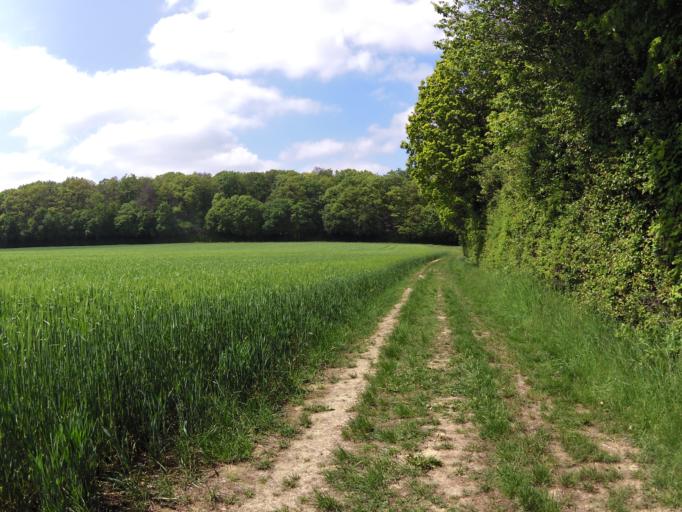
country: DE
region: Bavaria
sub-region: Regierungsbezirk Unterfranken
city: Reichenberg
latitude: 49.7408
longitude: 9.9045
